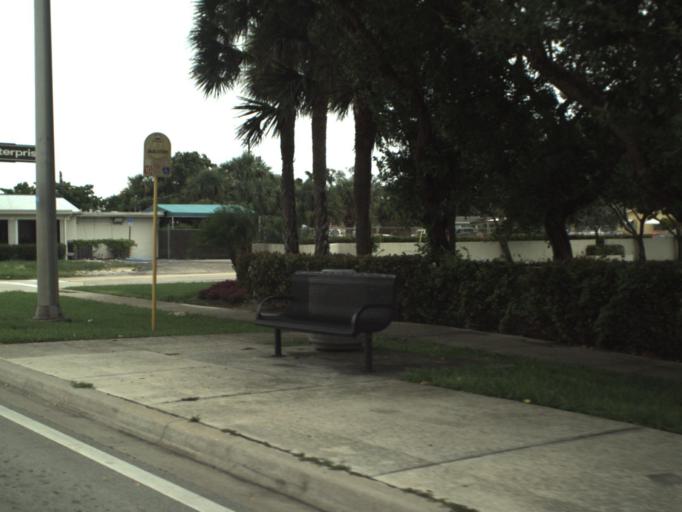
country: US
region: Florida
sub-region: Broward County
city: Terra Mar
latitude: 26.2280
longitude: -80.1025
